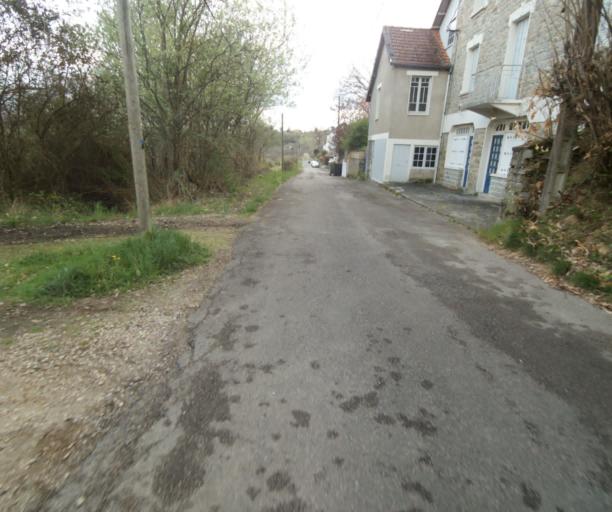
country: FR
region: Limousin
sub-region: Departement de la Correze
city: Tulle
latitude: 45.2564
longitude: 1.7409
